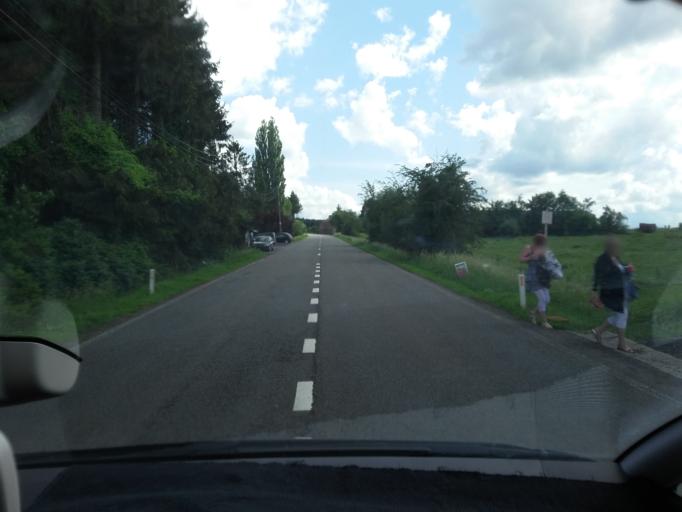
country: BE
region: Wallonia
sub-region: Province de Namur
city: Rochefort
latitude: 50.1442
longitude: 5.2205
